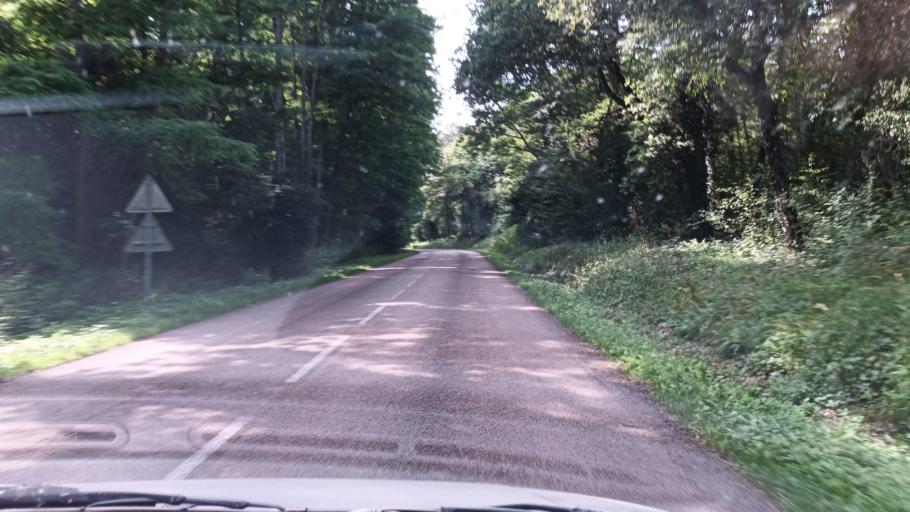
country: FR
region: Bourgogne
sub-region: Departement de l'Yonne
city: Villeneuve-sur-Yonne
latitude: 48.0751
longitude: 3.2683
